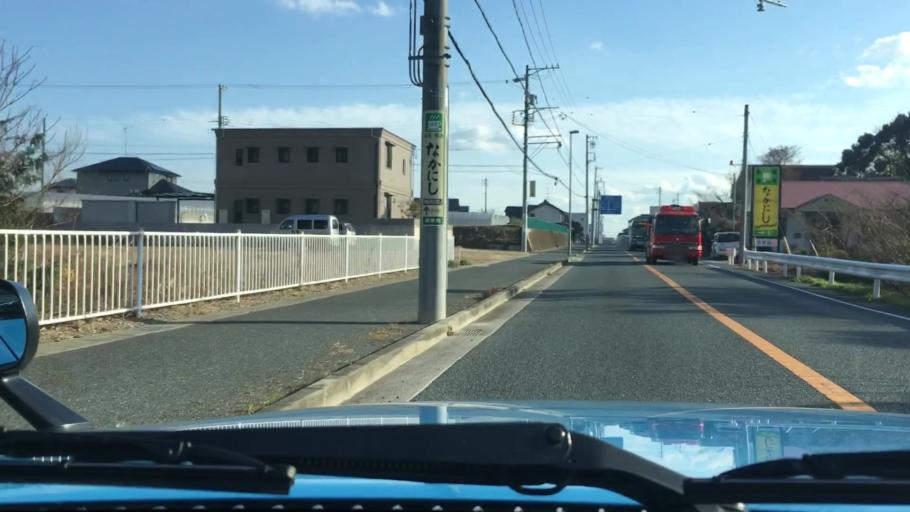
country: JP
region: Shizuoka
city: Hamamatsu
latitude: 34.7573
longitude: 137.6689
